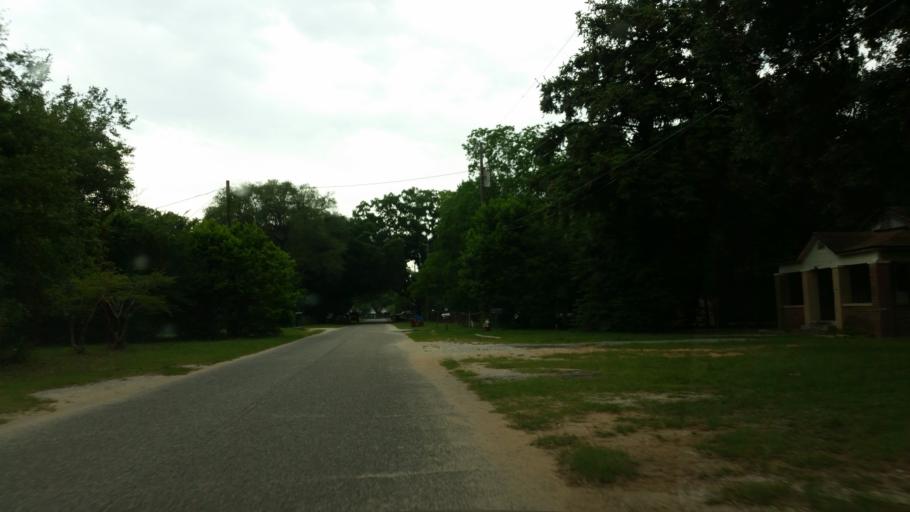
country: US
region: Florida
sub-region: Escambia County
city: Brent
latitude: 30.4693
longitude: -87.2219
